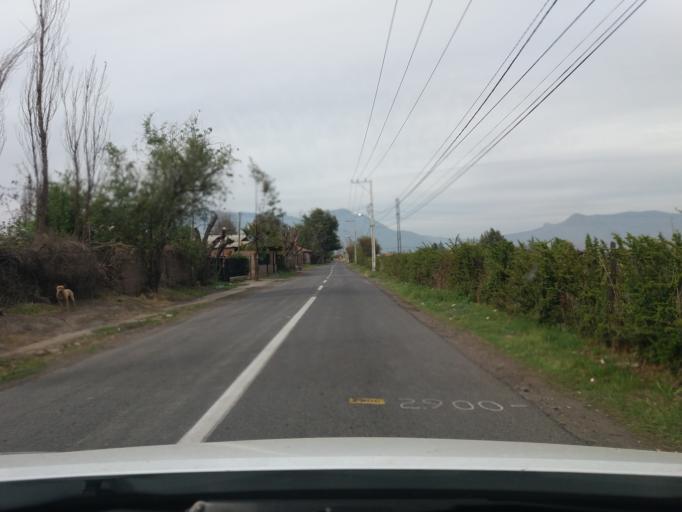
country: CL
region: Valparaiso
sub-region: Provincia de Los Andes
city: Los Andes
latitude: -32.8260
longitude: -70.6586
